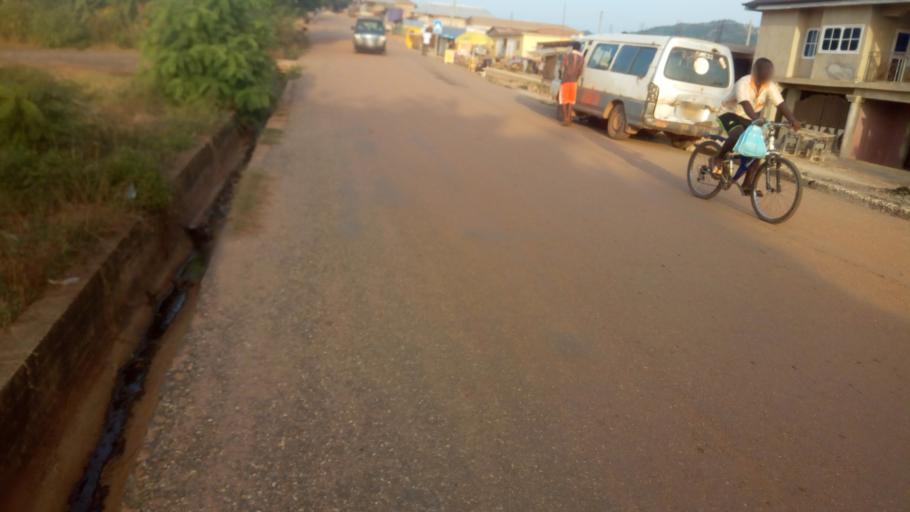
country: GH
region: Ashanti
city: Obuasi
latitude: 6.2129
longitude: -1.6964
